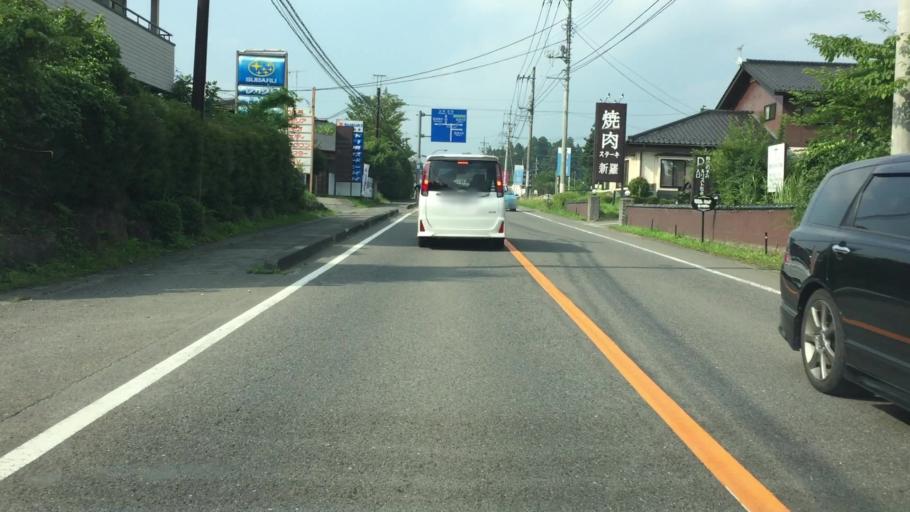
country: JP
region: Tochigi
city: Kuroiso
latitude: 37.0542
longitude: 140.0356
